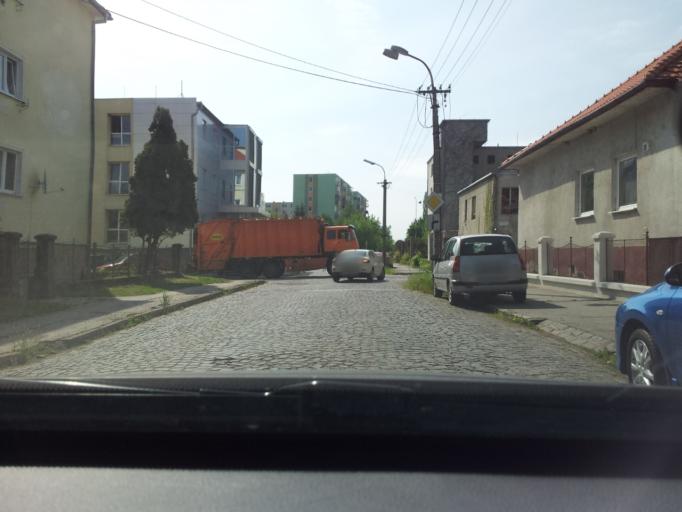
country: SK
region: Nitriansky
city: Levice
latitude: 48.2164
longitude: 18.5945
